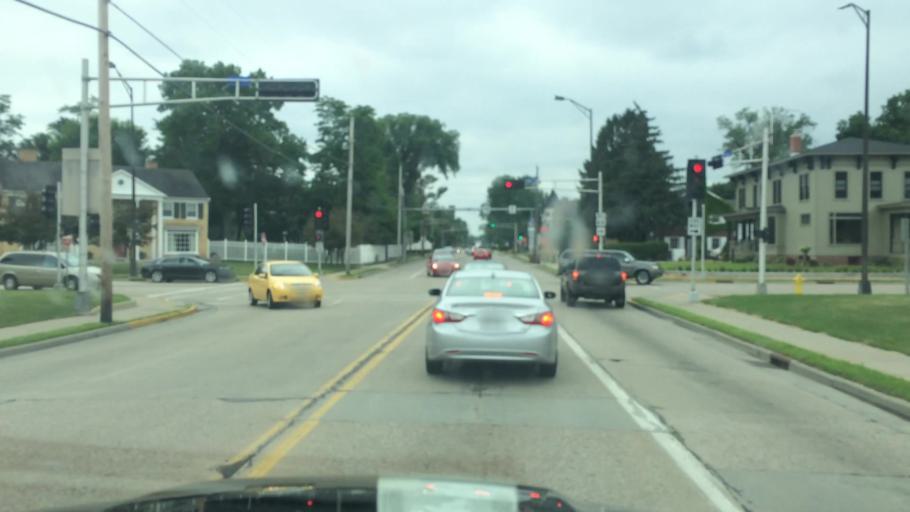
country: US
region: Wisconsin
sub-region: Portage County
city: Stevens Point
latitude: 44.5239
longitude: -89.5749
